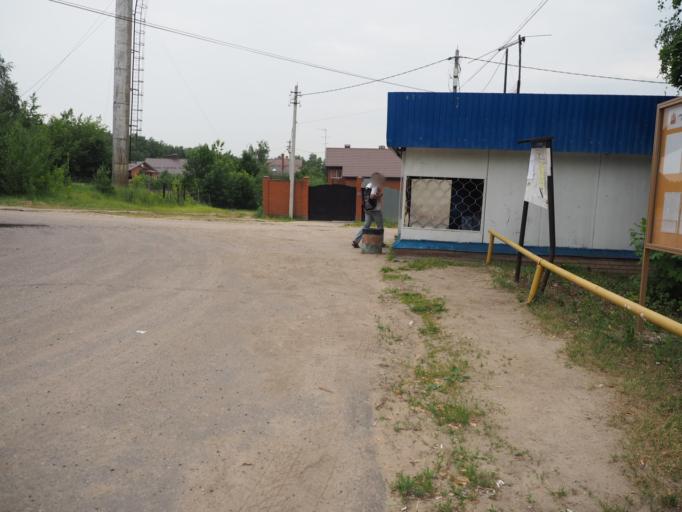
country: RU
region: Moskovskaya
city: Dzerzhinskiy
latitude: 55.6443
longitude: 37.8834
